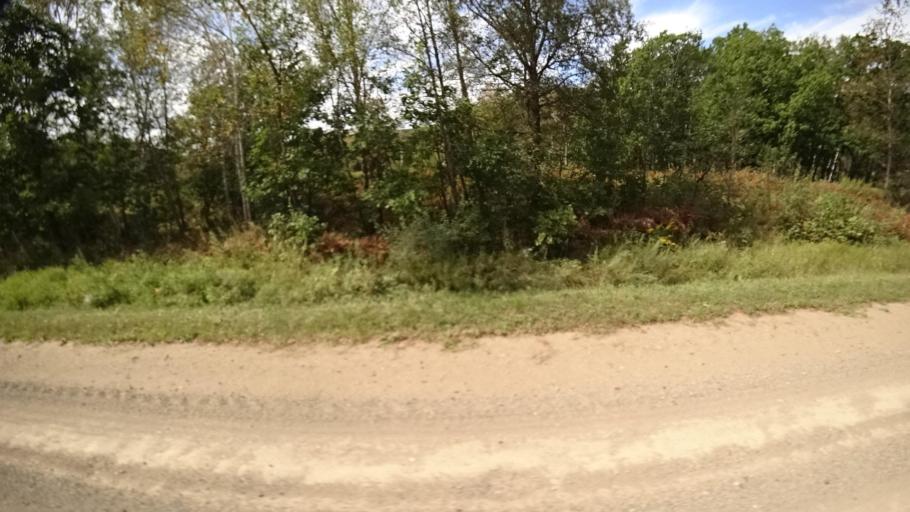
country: RU
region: Primorskiy
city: Yakovlevka
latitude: 44.6923
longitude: 133.6190
